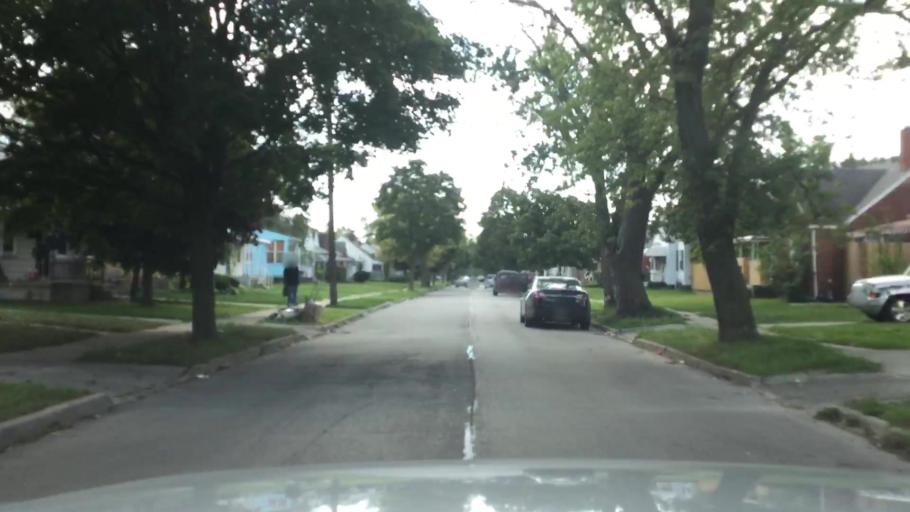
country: US
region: Michigan
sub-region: Wayne County
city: Dearborn Heights
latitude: 42.3417
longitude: -83.2242
